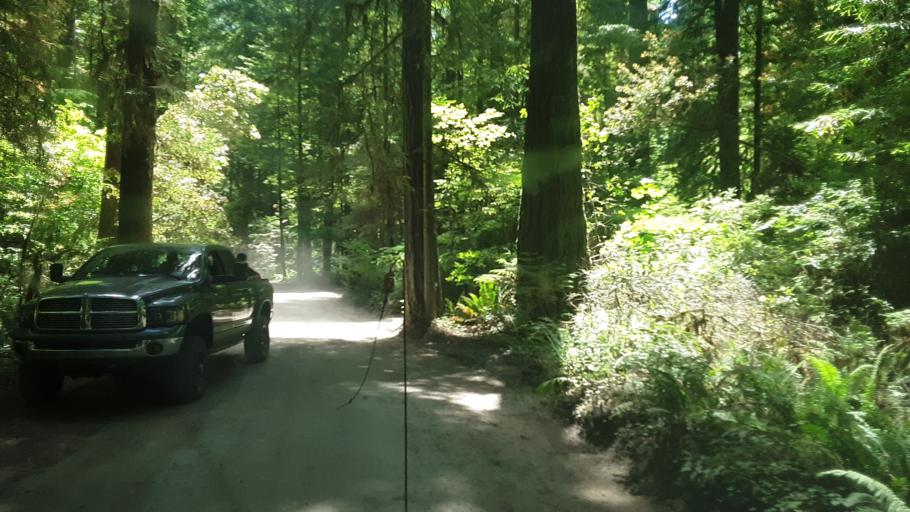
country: US
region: California
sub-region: Del Norte County
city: Bertsch-Oceanview
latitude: 41.8201
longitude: -124.1097
